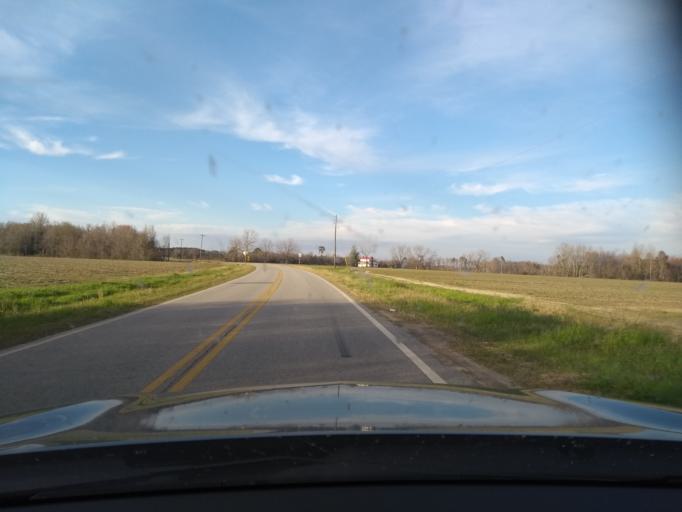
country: US
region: Georgia
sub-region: Bulloch County
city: Brooklet
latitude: 32.2992
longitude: -81.7732
